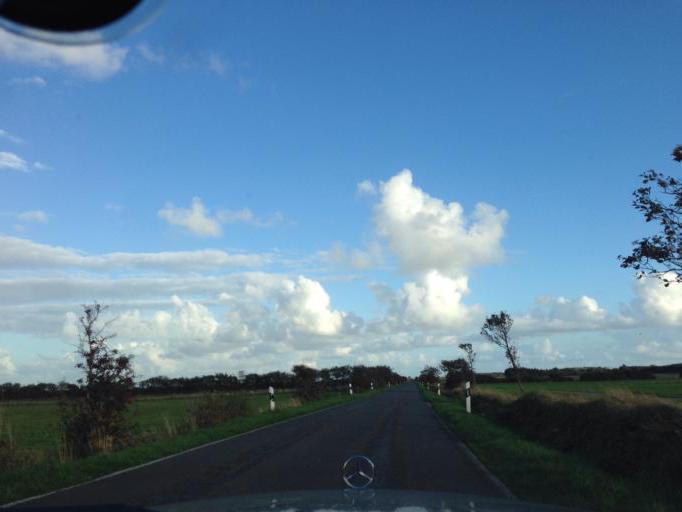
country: DE
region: Schleswig-Holstein
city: Utersum
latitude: 54.7138
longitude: 8.4123
